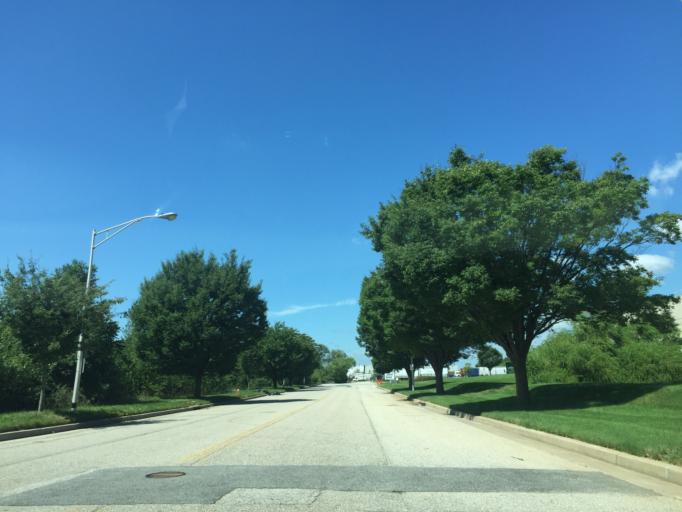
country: US
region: Maryland
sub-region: Baltimore County
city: Dundalk
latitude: 39.2675
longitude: -76.5377
